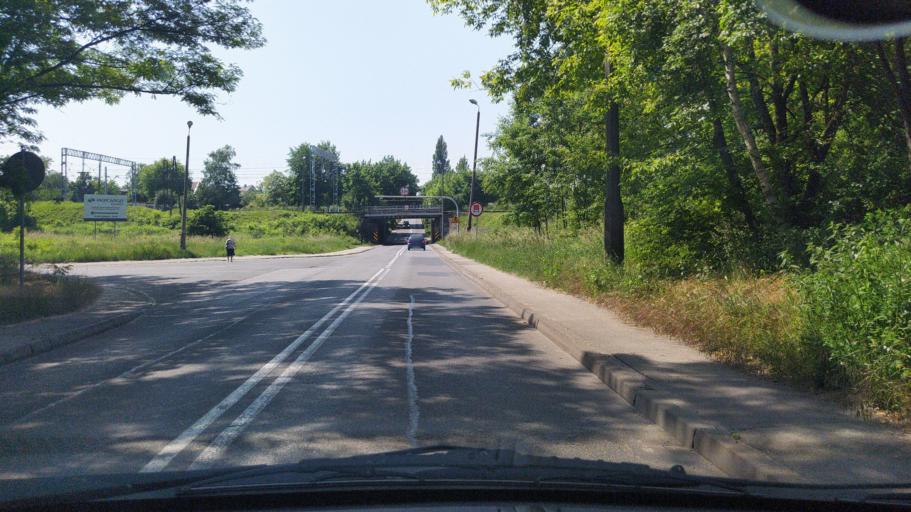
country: PL
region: Silesian Voivodeship
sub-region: Powiat gliwicki
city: Przyszowice
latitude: 50.2969
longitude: 18.7323
